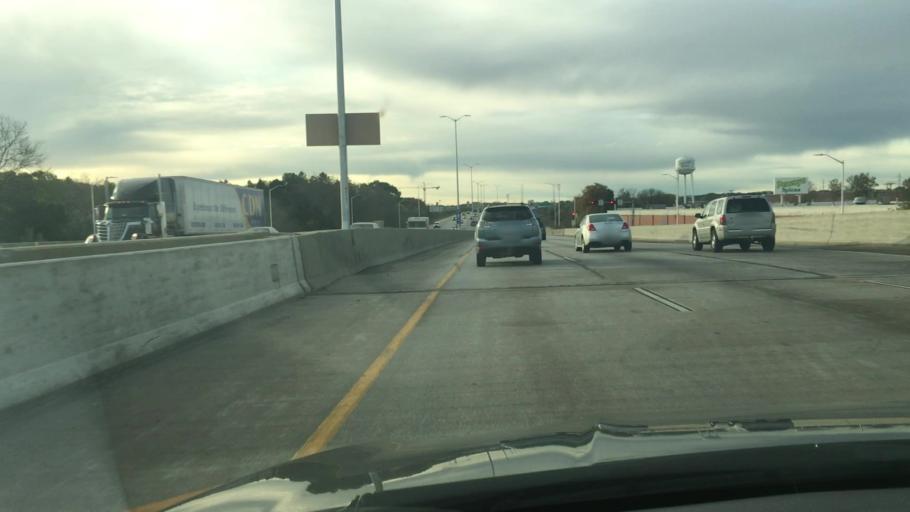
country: US
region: Wisconsin
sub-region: Waukesha County
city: Butler
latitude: 43.0887
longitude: -88.0580
